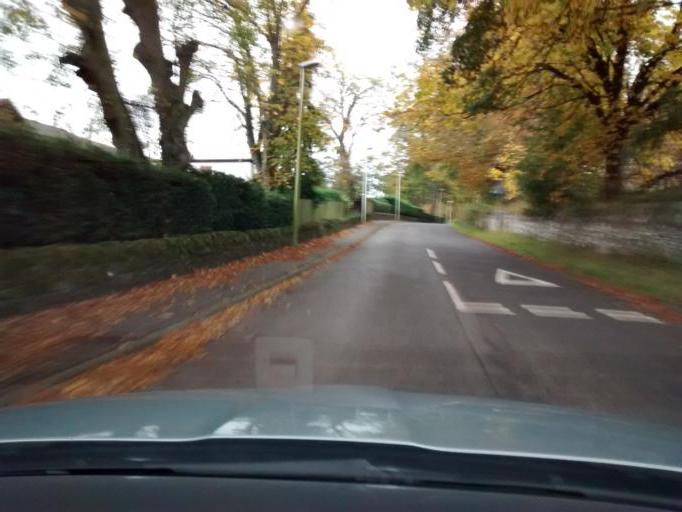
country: GB
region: Scotland
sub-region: Perth and Kinross
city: Auchterarder
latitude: 56.2969
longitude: -3.6932
